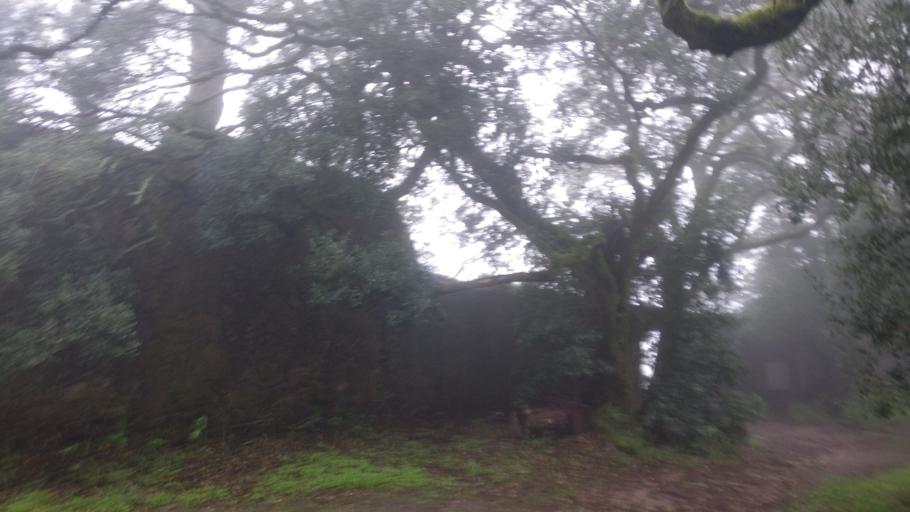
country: PT
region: Aveiro
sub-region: Mealhada
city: Pampilhosa do Botao
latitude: 40.3755
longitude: -8.3705
